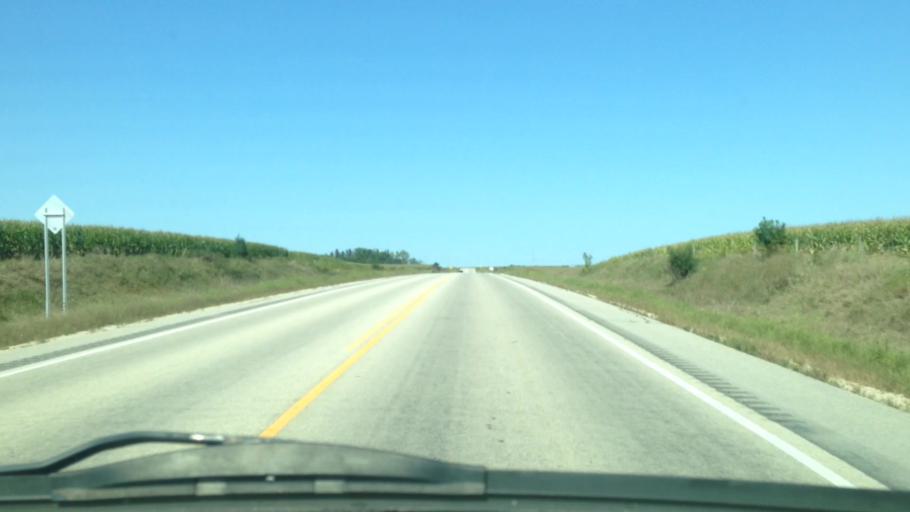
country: US
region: Minnesota
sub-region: Fillmore County
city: Rushford
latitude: 43.8556
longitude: -91.7458
